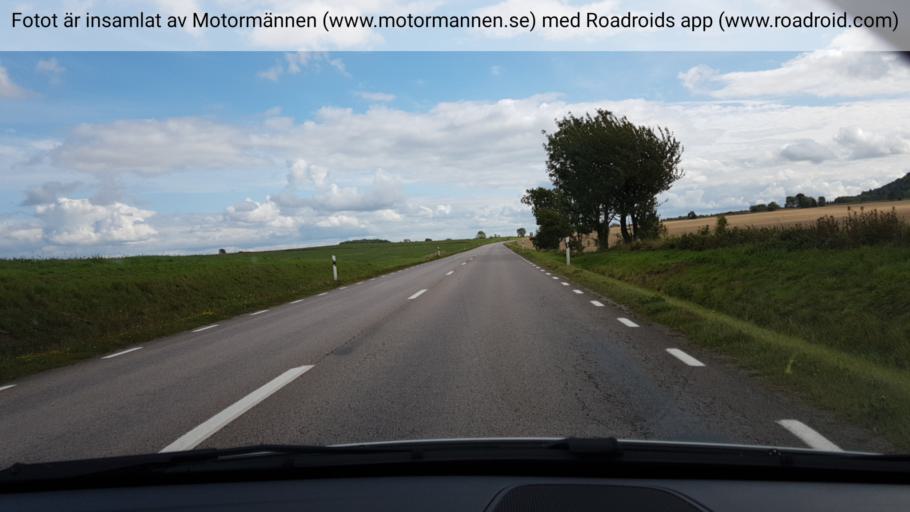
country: SE
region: Vaestra Goetaland
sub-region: Falkopings Kommun
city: Falkoeping
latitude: 58.1547
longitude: 13.5924
